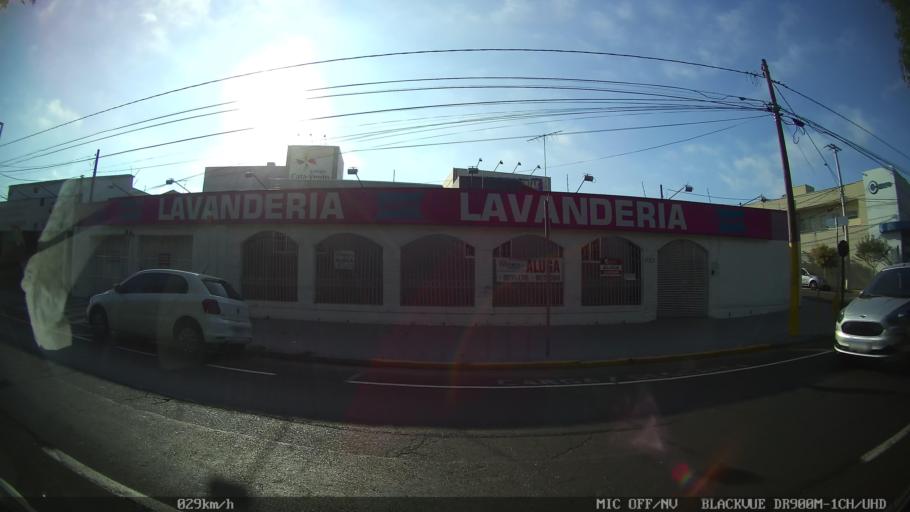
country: BR
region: Sao Paulo
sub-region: Sao Jose Do Rio Preto
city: Sao Jose do Rio Preto
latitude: -20.8177
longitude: -49.3656
